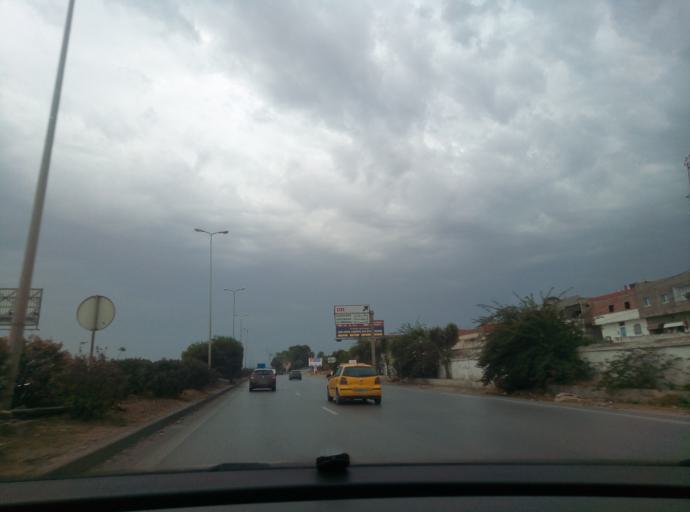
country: TN
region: Bin 'Arus
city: Ben Arous
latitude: 36.7502
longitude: 10.2062
